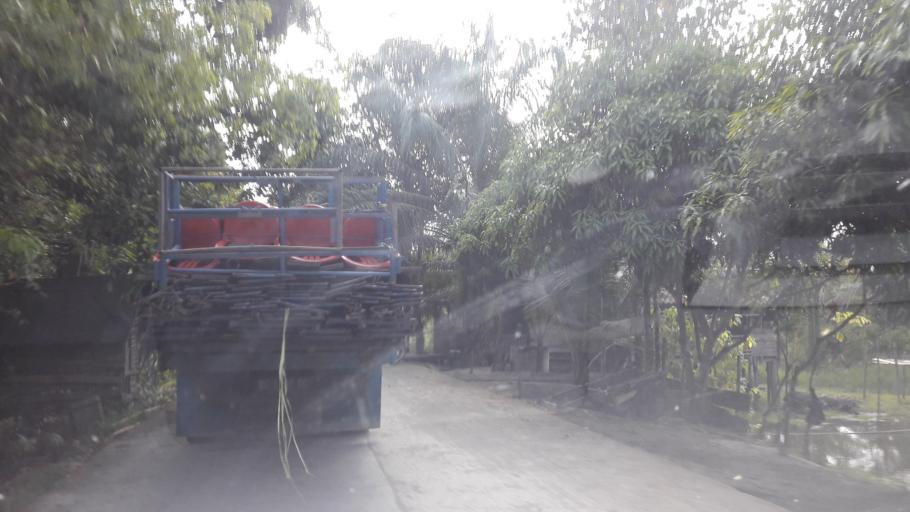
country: ID
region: South Sumatra
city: Gunungmenang
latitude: -3.1086
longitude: 103.9607
